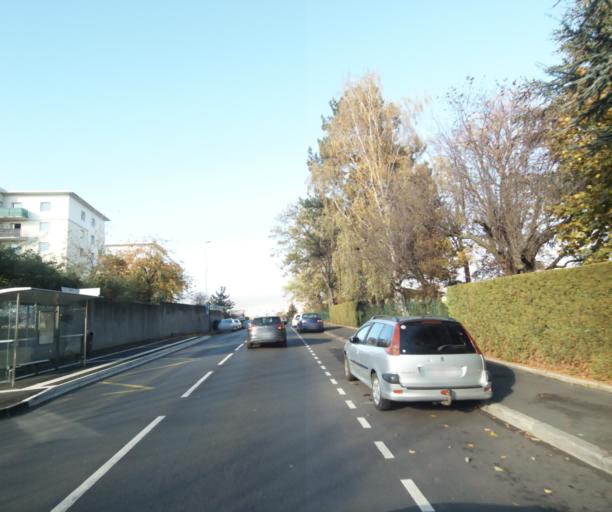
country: FR
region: Auvergne
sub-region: Departement du Puy-de-Dome
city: Aubiere
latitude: 45.7699
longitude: 3.1107
